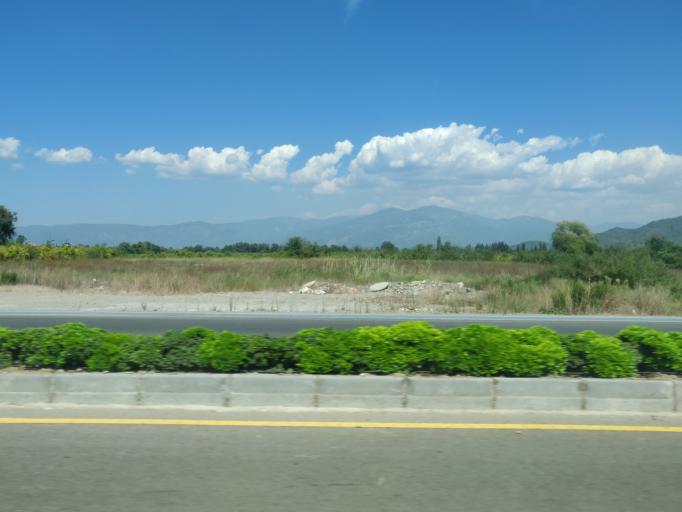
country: TR
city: Dalyan
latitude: 36.8383
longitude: 28.6622
